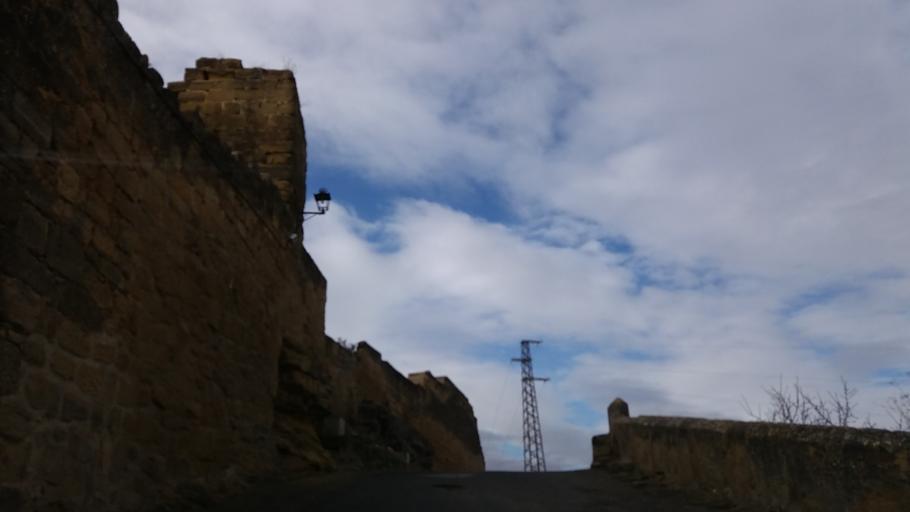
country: ES
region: La Rioja
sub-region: Provincia de La Rioja
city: Briones
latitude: 42.5455
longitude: -2.7855
